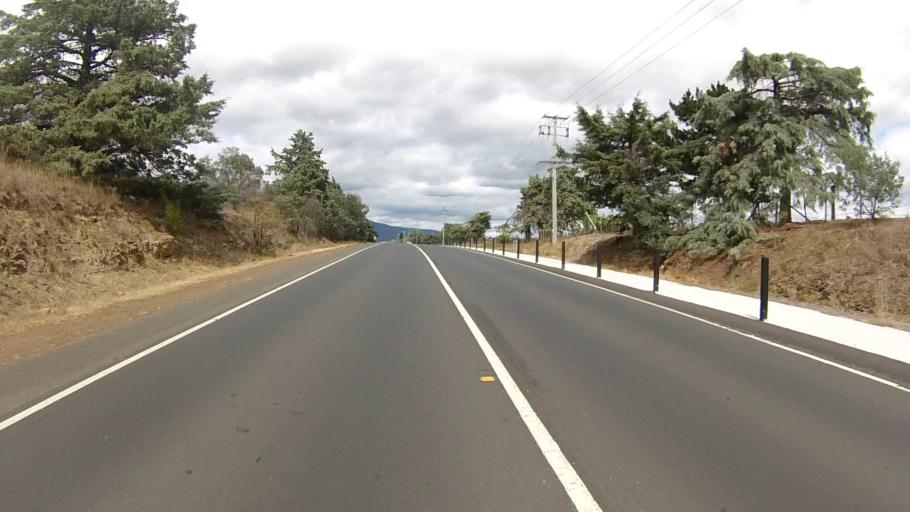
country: AU
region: Tasmania
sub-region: Brighton
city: Bridgewater
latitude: -42.6895
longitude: 147.2610
